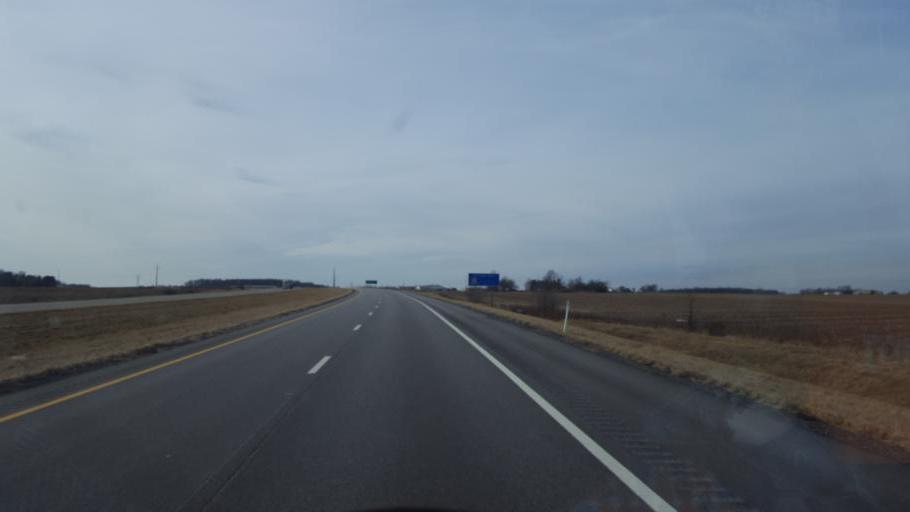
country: US
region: Ohio
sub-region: Wayne County
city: Apple Creek
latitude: 40.8091
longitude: -81.8330
